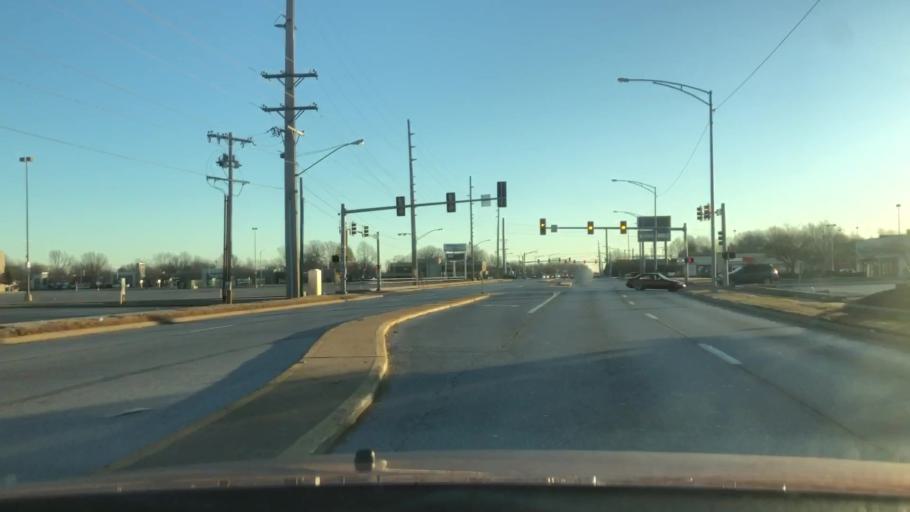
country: US
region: Missouri
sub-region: Greene County
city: Springfield
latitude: 37.1594
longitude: -93.2660
